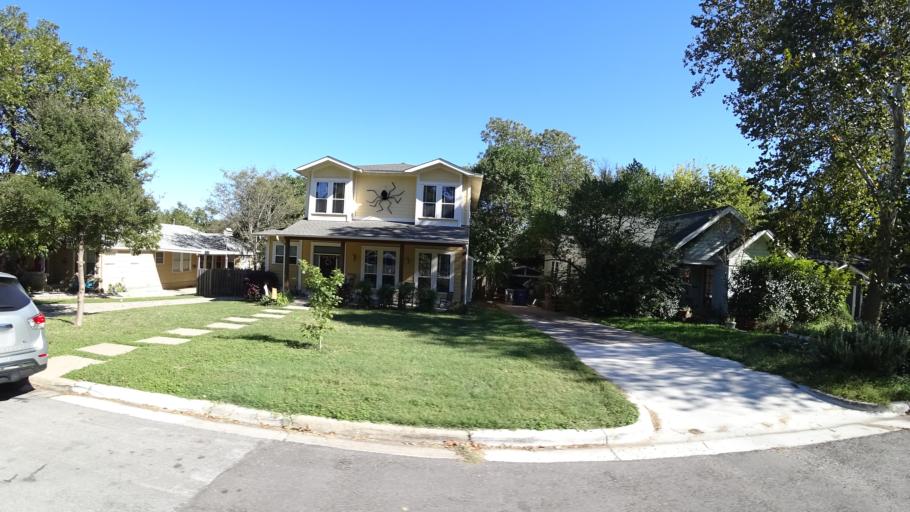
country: US
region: Texas
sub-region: Travis County
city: Austin
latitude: 30.3132
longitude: -97.7513
